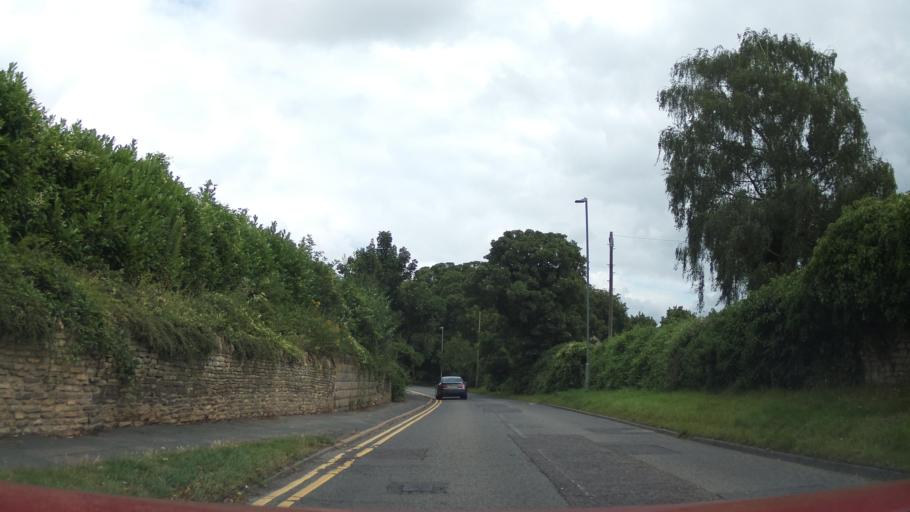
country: GB
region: England
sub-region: Lincolnshire
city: Stamford
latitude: 52.6540
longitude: -0.4676
